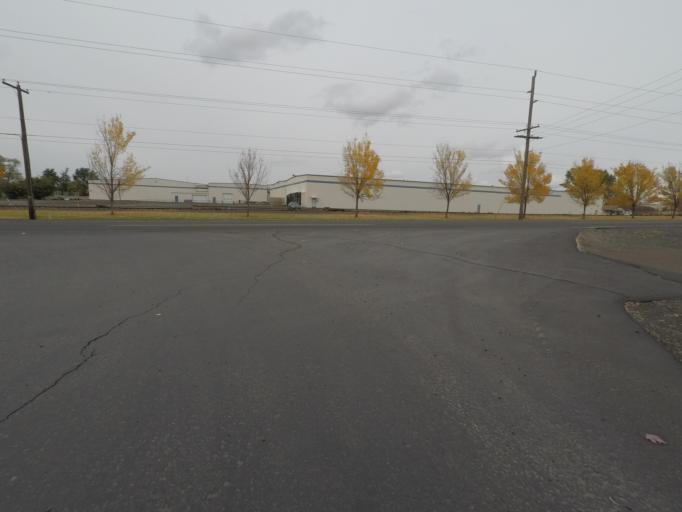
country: US
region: Washington
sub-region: Walla Walla County
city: Walla Walla East
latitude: 46.0820
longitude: -118.2749
